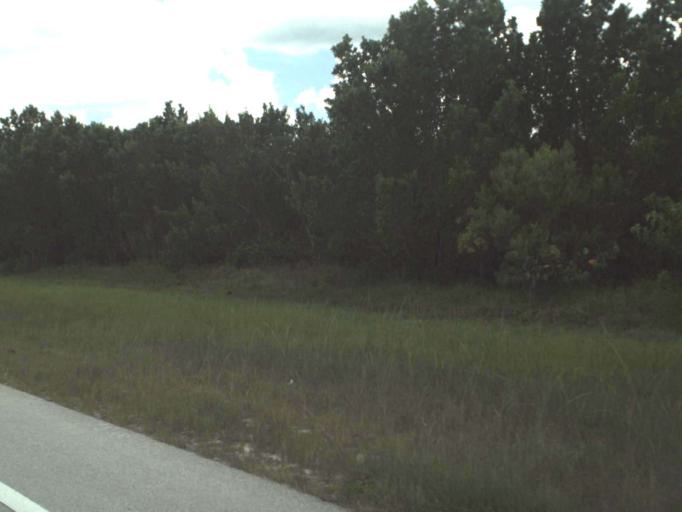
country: US
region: Florida
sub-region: Saint Lucie County
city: Indian River Estates
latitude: 27.4131
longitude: -80.2737
